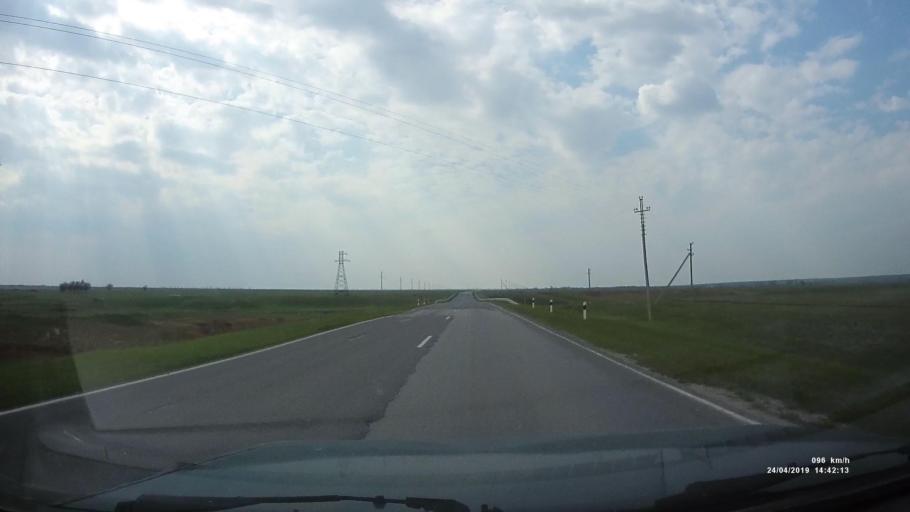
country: RU
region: Rostov
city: Remontnoye
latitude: 46.4509
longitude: 43.8665
